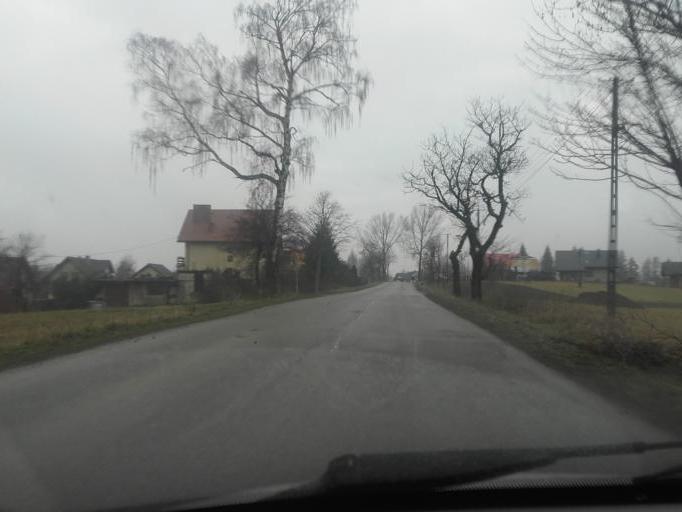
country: PL
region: Silesian Voivodeship
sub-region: Powiat cieszynski
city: Istebna
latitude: 49.5535
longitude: 18.9214
